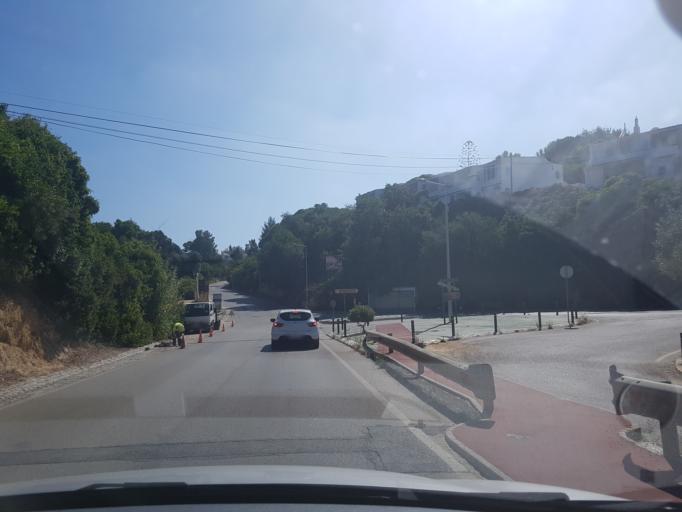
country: PT
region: Faro
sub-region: Lagoa
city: Carvoeiro
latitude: 37.0926
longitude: -8.4521
